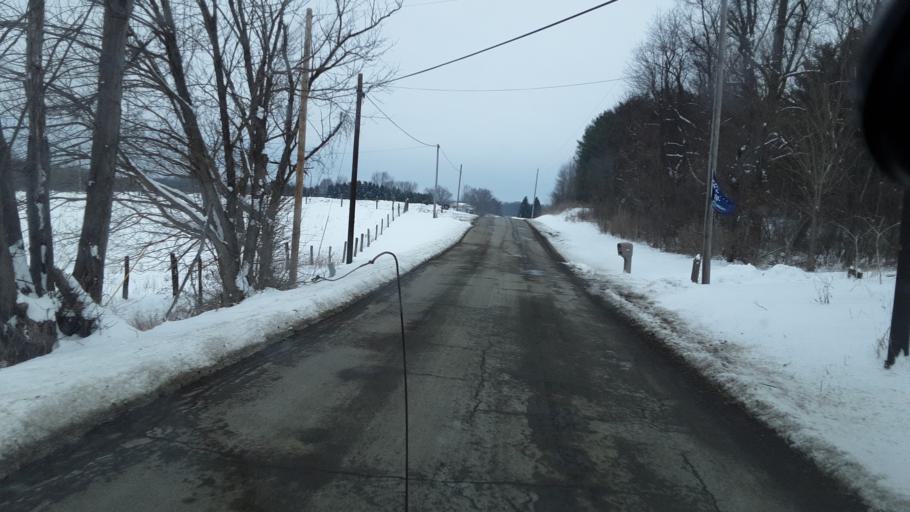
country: US
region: Ohio
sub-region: Muskingum County
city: Roseville
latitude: 39.9322
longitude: -82.1778
